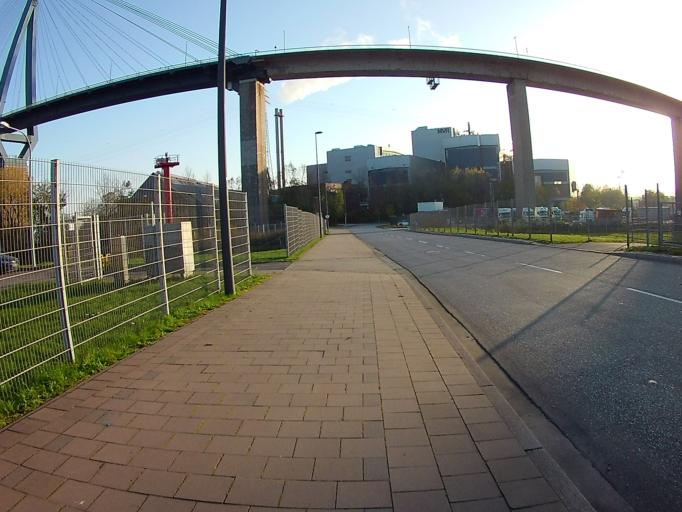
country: DE
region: Hamburg
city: Altona
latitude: 53.5234
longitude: 9.9345
